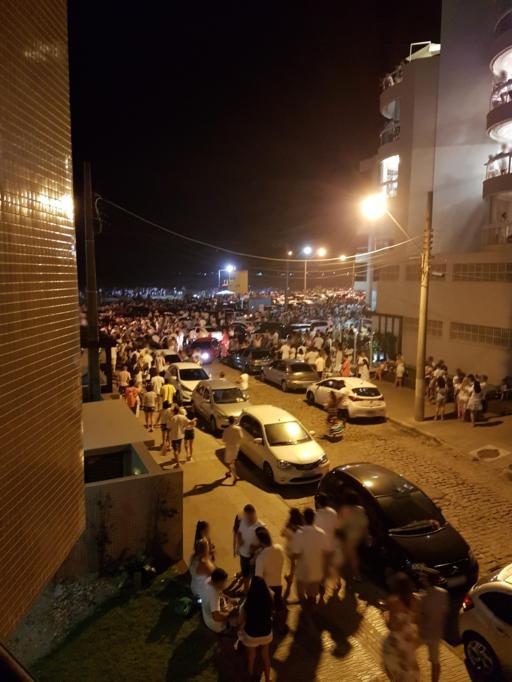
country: BR
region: Santa Catarina
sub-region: Laguna
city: Laguna
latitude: -28.4872
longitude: -48.7664
